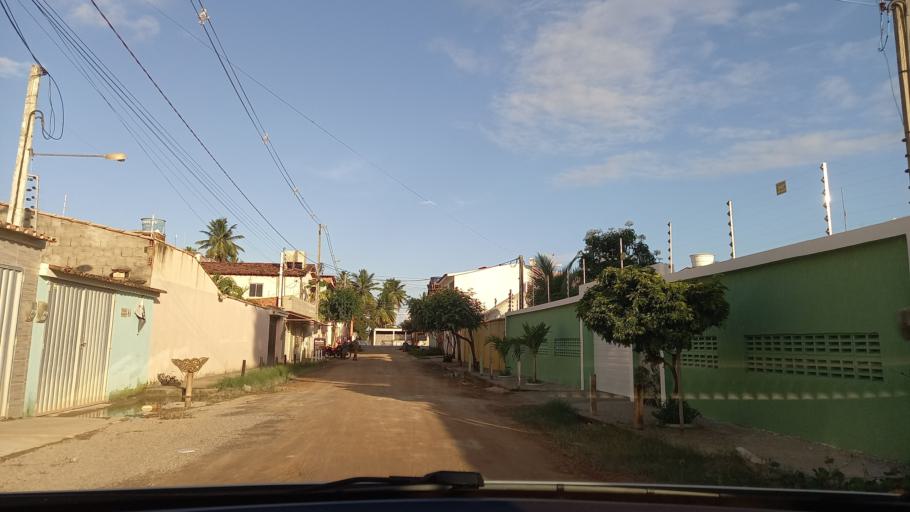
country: BR
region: Pernambuco
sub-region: Sao Jose Da Coroa Grande
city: Sao Jose da Coroa Grande
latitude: -8.9233
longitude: -35.1603
